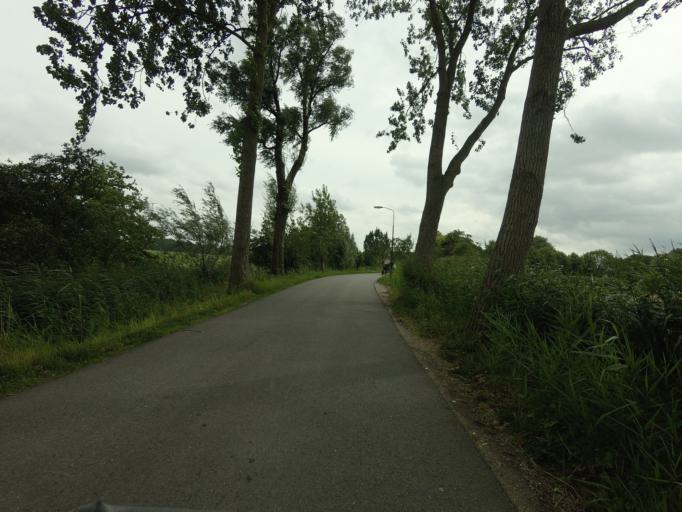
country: NL
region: North Holland
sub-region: Gemeente Amsterdam
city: Driemond
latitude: 52.2814
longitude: 5.0050
